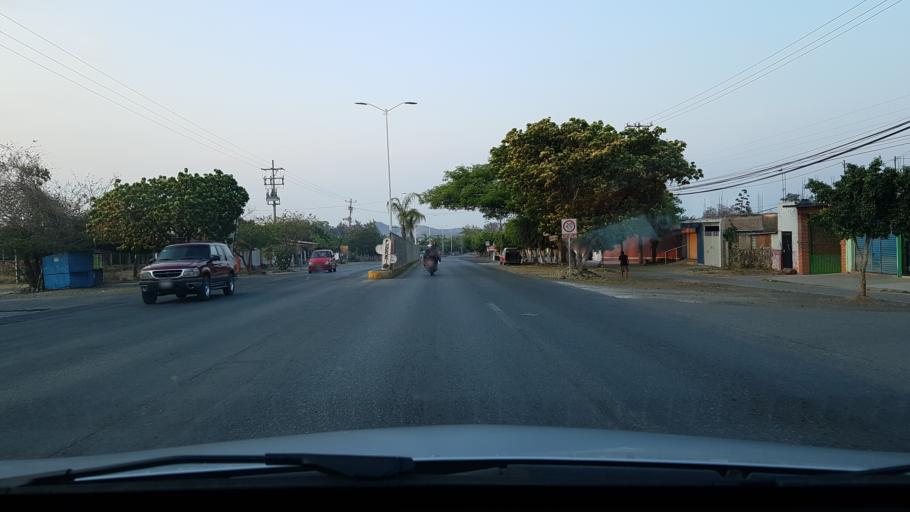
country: MX
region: Morelos
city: Jonacatepec de Leandro Valle
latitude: 18.6931
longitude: -98.8018
